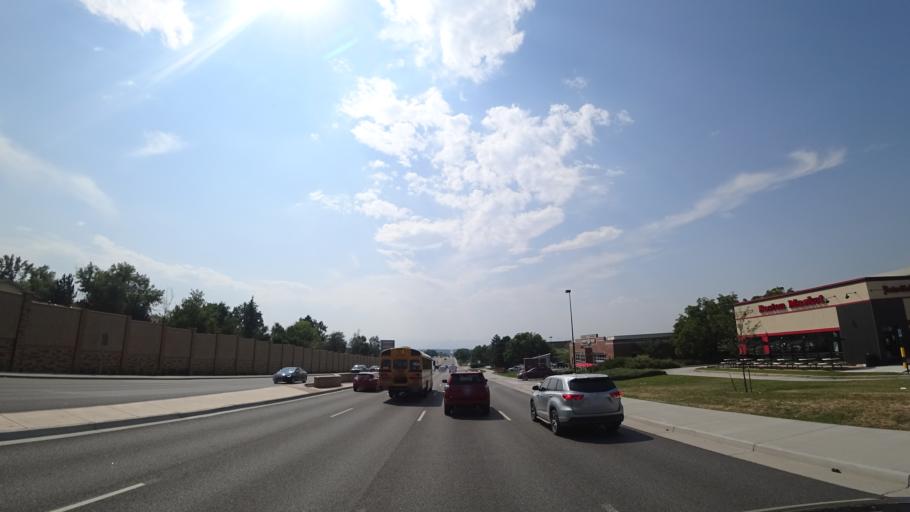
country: US
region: Colorado
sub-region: Arapahoe County
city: Castlewood
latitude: 39.5951
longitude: -104.8908
